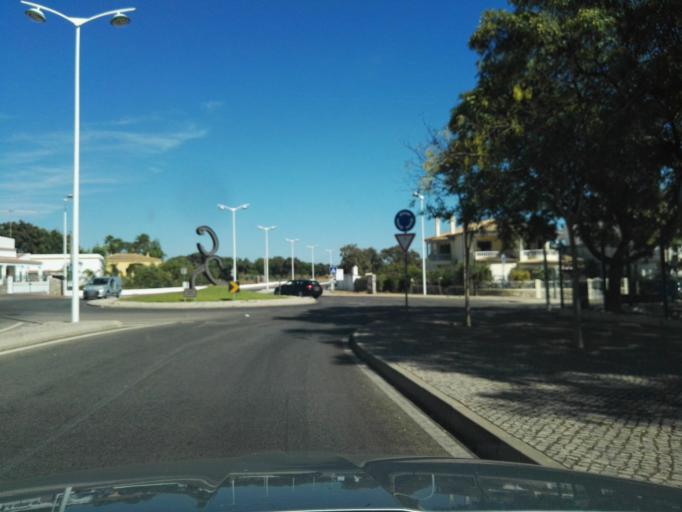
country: PT
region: Faro
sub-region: Sao Bras de Alportel
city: Sao Bras de Alportel
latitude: 37.1592
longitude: -7.8858
